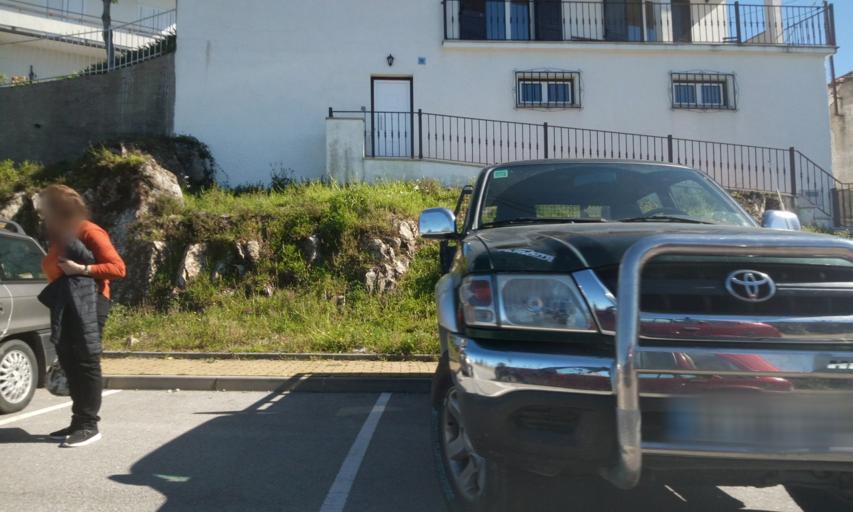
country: PT
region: Guarda
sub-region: Manteigas
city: Manteigas
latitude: 40.4924
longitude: -7.5900
